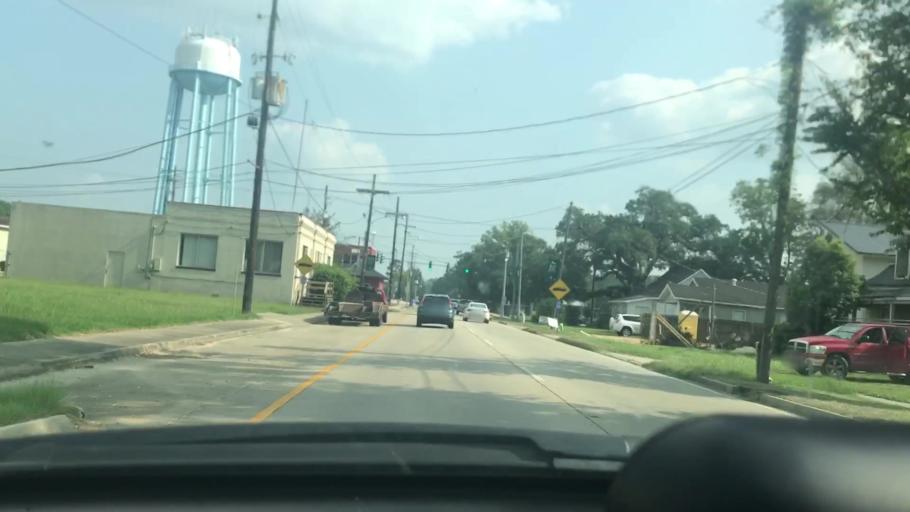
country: US
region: Louisiana
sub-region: Tangipahoa Parish
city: Hammond
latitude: 30.5019
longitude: -90.4617
